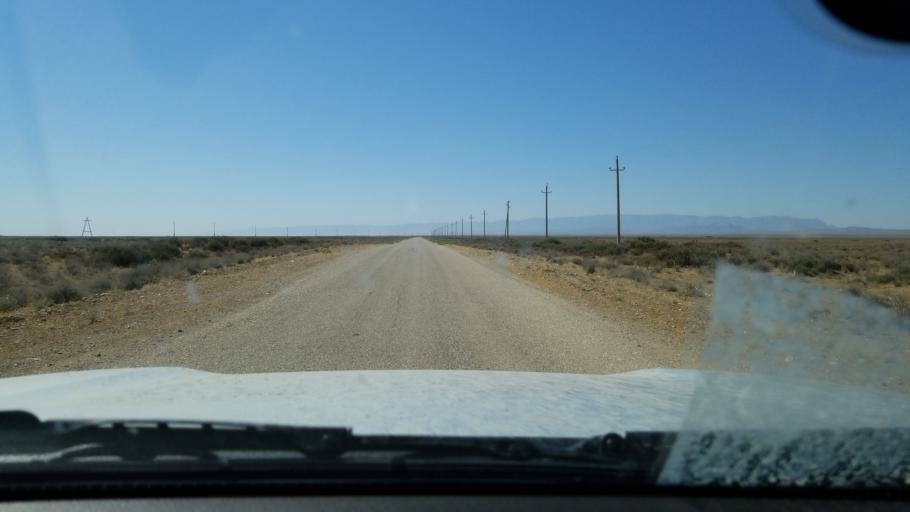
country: TM
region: Balkan
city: Balkanabat
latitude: 40.1179
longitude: 54.3835
